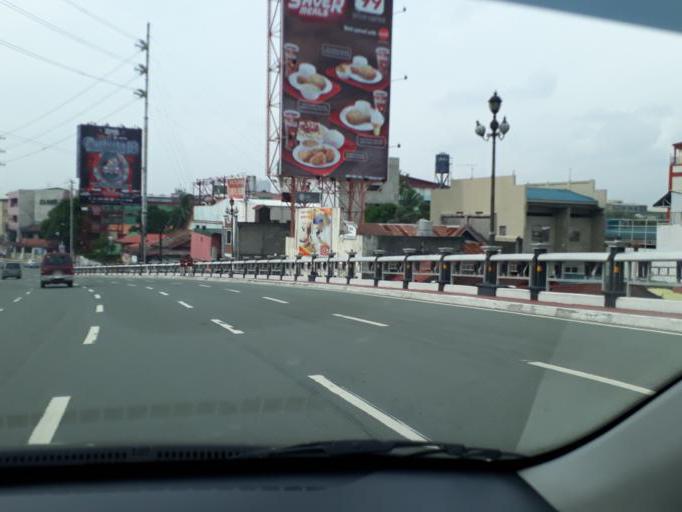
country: PH
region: Metro Manila
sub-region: City of Manila
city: Quiapo
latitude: 14.5970
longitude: 121.0014
